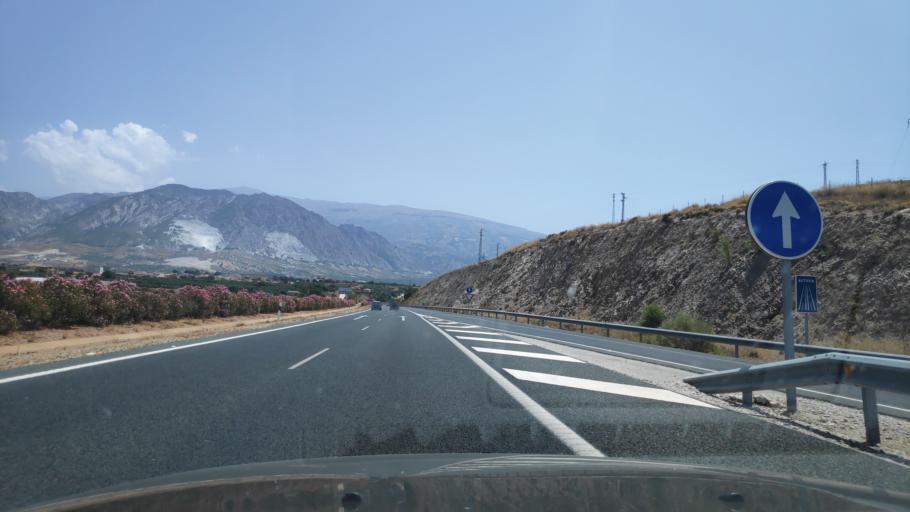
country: ES
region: Andalusia
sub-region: Provincia de Granada
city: Durcal
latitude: 36.9878
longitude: -3.6038
